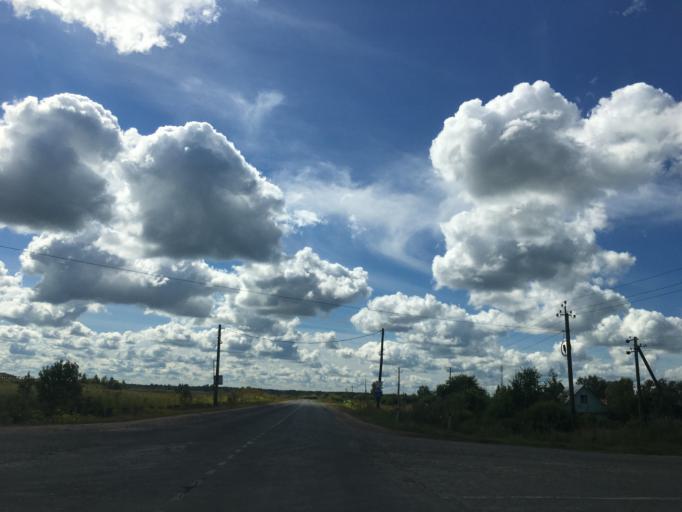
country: RU
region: Pskov
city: Pskov
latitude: 57.7455
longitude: 28.1578
